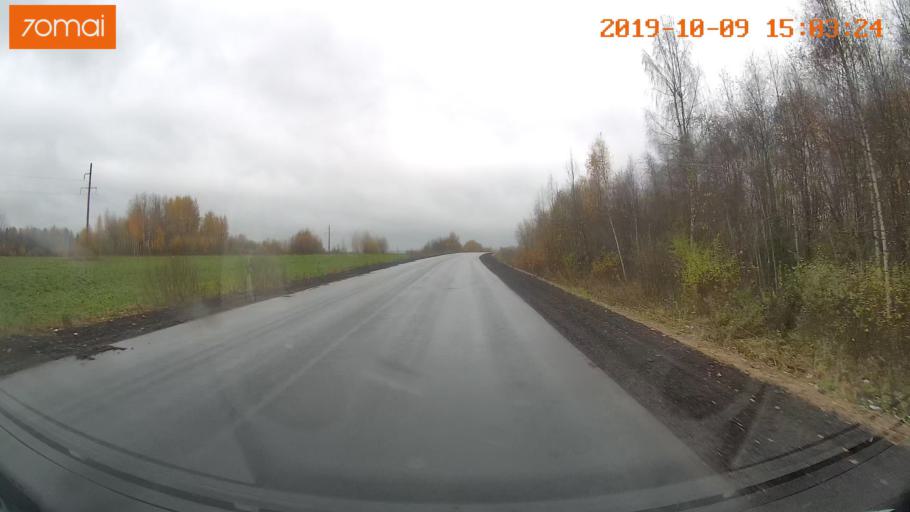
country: RU
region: Kostroma
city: Chistyye Bory
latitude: 58.2717
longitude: 41.6759
